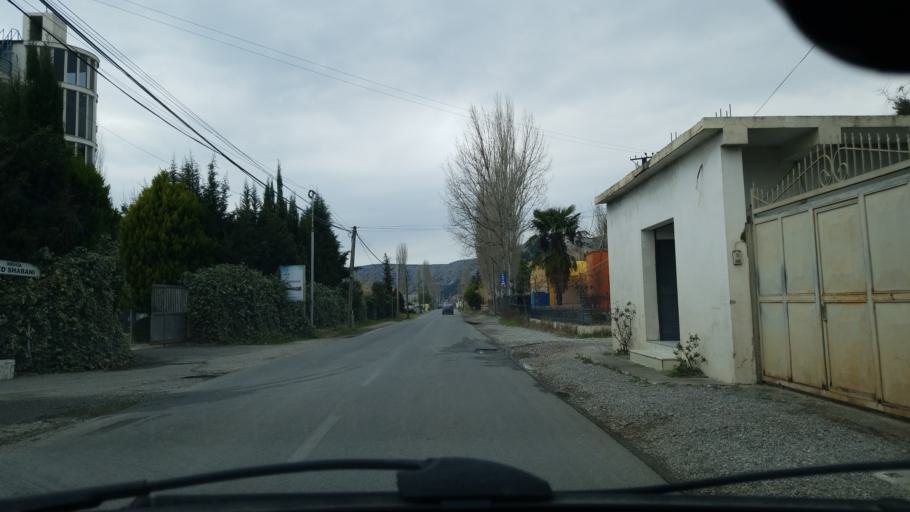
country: AL
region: Lezhe
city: Lezhe
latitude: 41.7816
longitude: 19.6310
